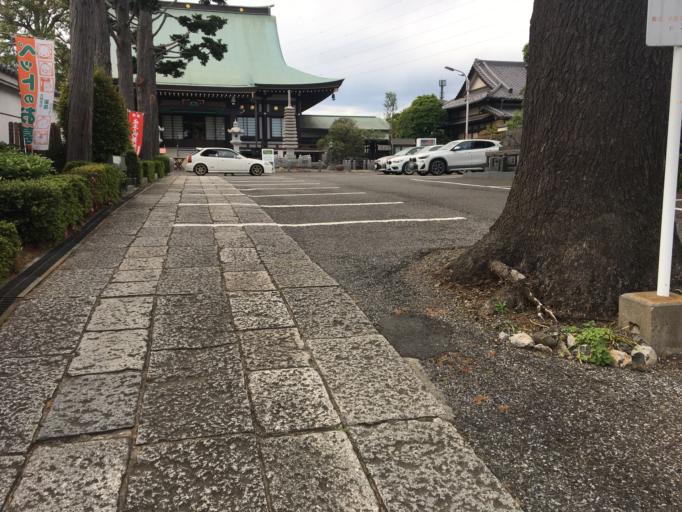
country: JP
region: Saitama
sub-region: Kawaguchi-shi
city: Hatogaya-honcho
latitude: 35.8451
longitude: 139.7393
